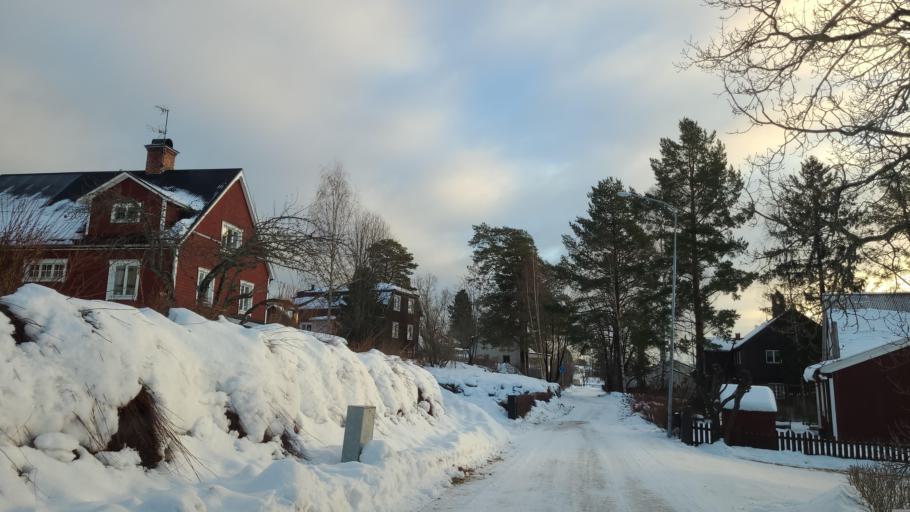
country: SE
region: Gaevleborg
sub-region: Bollnas Kommun
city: Bollnas
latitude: 61.3606
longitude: 16.4141
